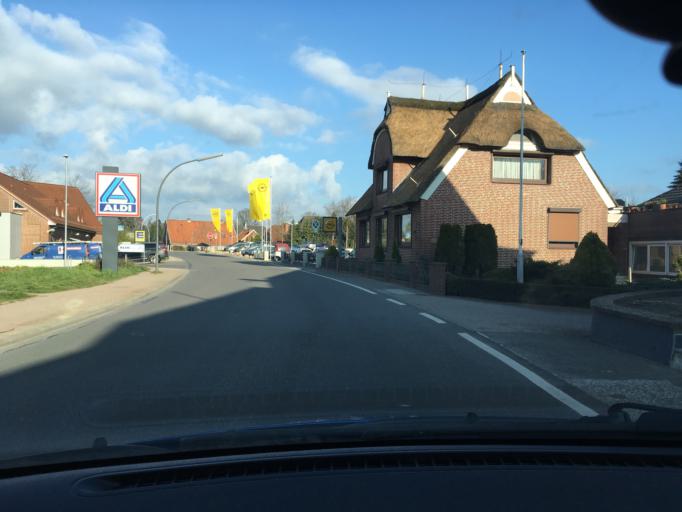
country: DE
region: Hamburg
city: Bergedorf
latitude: 53.4448
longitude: 10.2310
